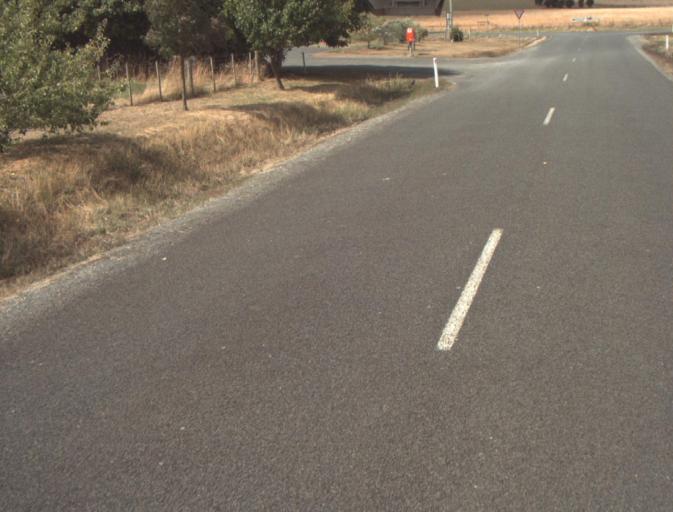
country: AU
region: Tasmania
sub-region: Launceston
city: Mayfield
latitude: -41.3102
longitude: 147.0497
